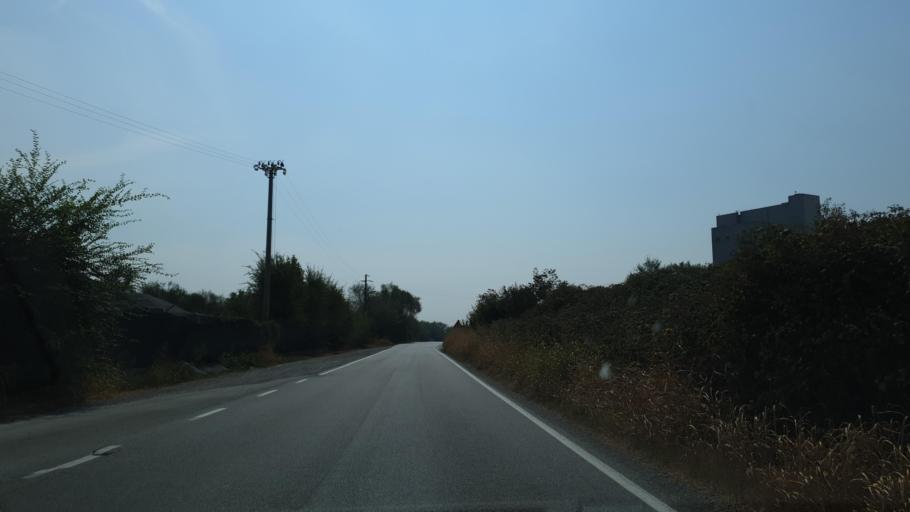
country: IT
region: Lombardy
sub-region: Provincia di Brescia
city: Montirone
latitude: 45.4332
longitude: 10.2578
